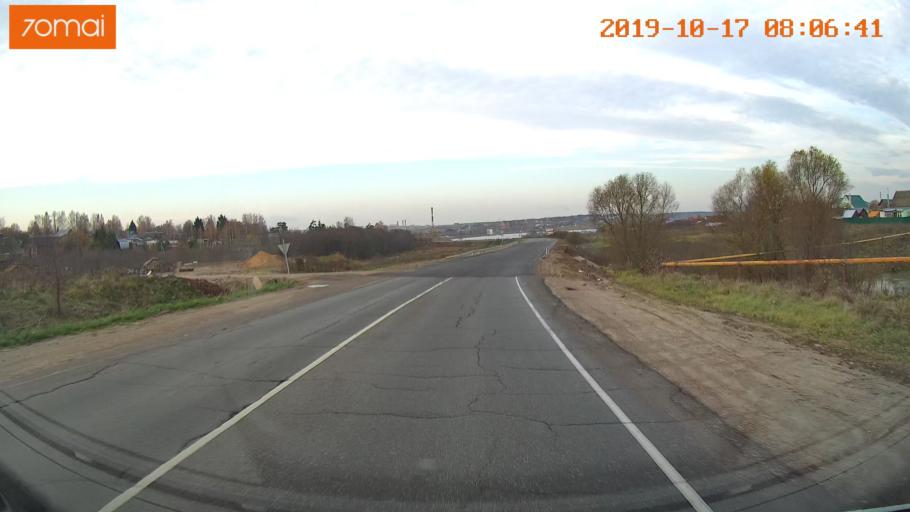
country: RU
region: Vladimir
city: Kol'chugino
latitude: 56.3201
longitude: 39.4113
